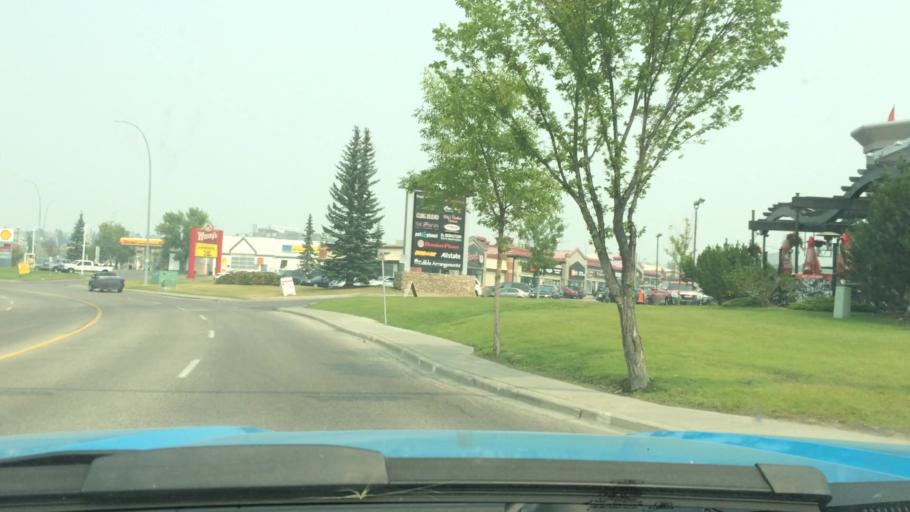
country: CA
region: Alberta
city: Calgary
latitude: 51.1266
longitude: -114.1979
